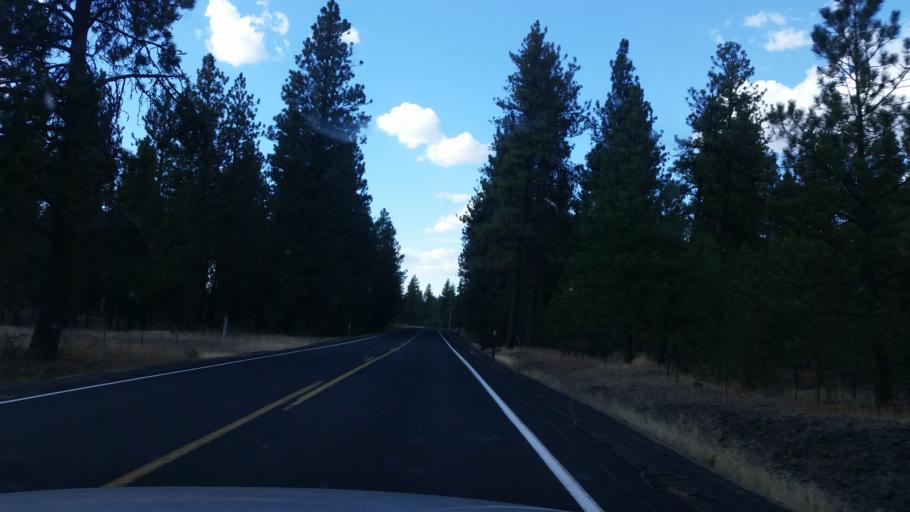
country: US
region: Washington
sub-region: Spokane County
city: Cheney
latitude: 47.4556
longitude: -117.5780
